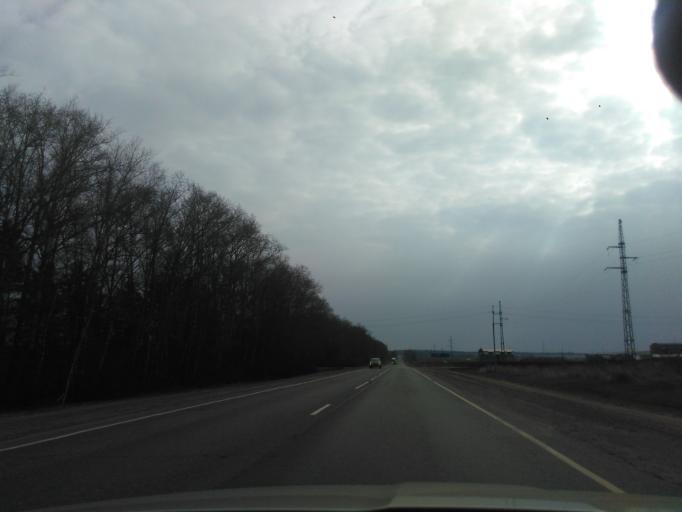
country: RU
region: Moskovskaya
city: Yermolino
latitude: 56.1354
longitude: 37.4040
